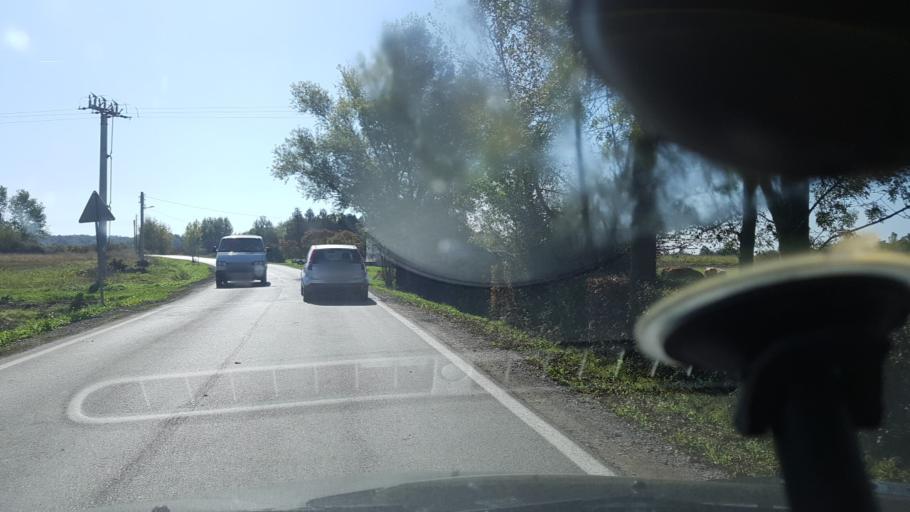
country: HR
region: Zagrebacka
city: Lupoglav
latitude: 45.7096
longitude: 16.3354
